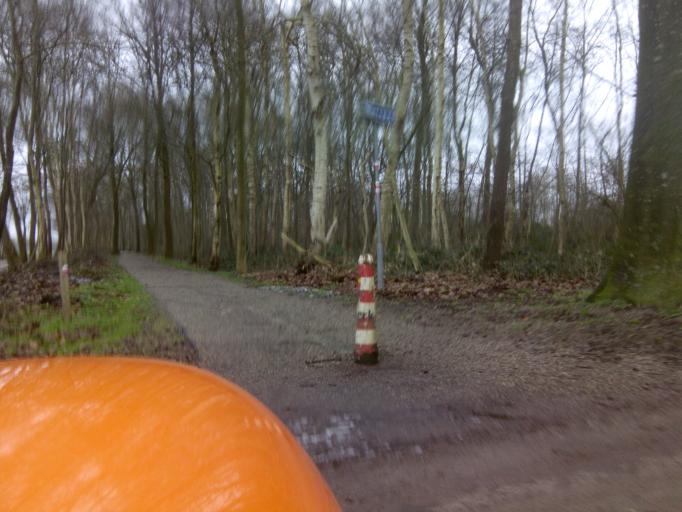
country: NL
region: Gelderland
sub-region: Gemeente Nijkerk
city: Nijkerk
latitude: 52.2238
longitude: 5.5267
